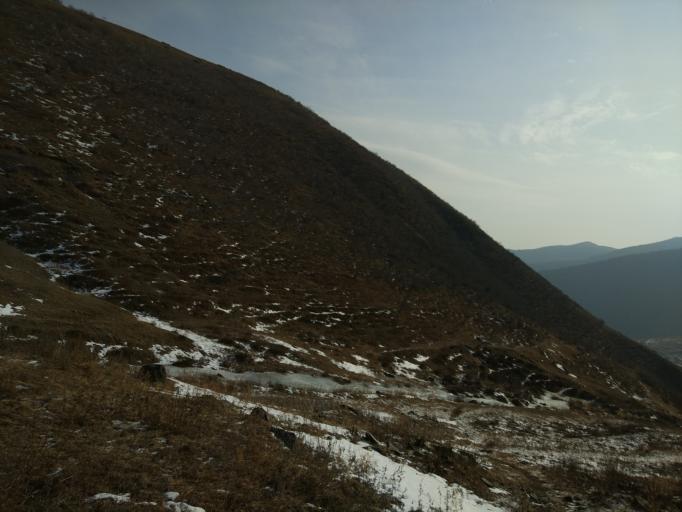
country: CN
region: Hebei
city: Xiwanzi
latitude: 40.8593
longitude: 115.4551
